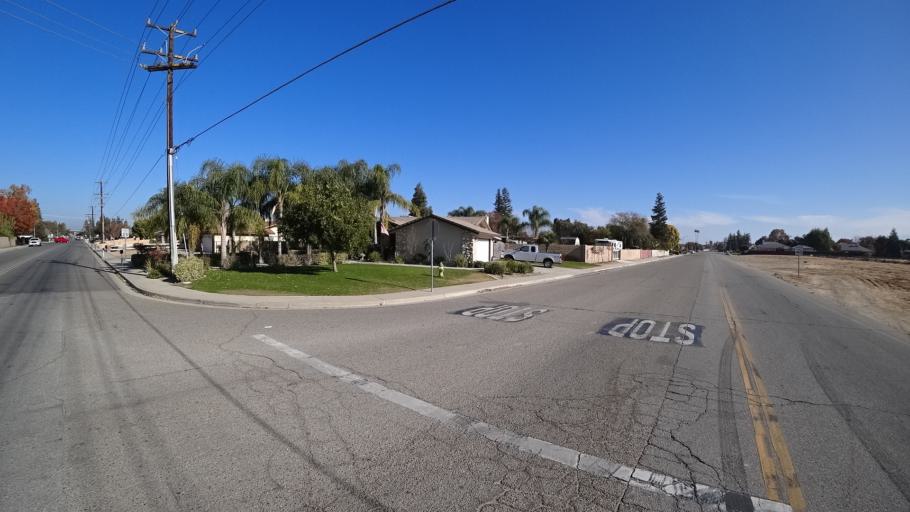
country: US
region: California
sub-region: Kern County
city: Rosedale
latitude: 35.3762
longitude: -119.1279
